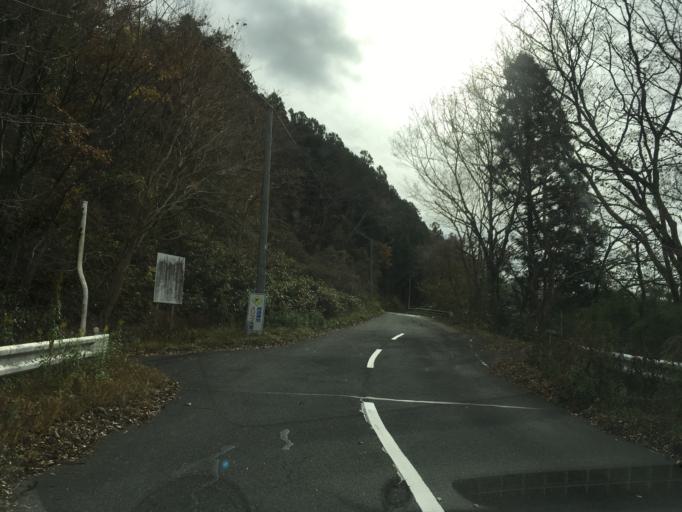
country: JP
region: Iwate
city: Ichinoseki
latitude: 38.7874
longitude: 141.2646
